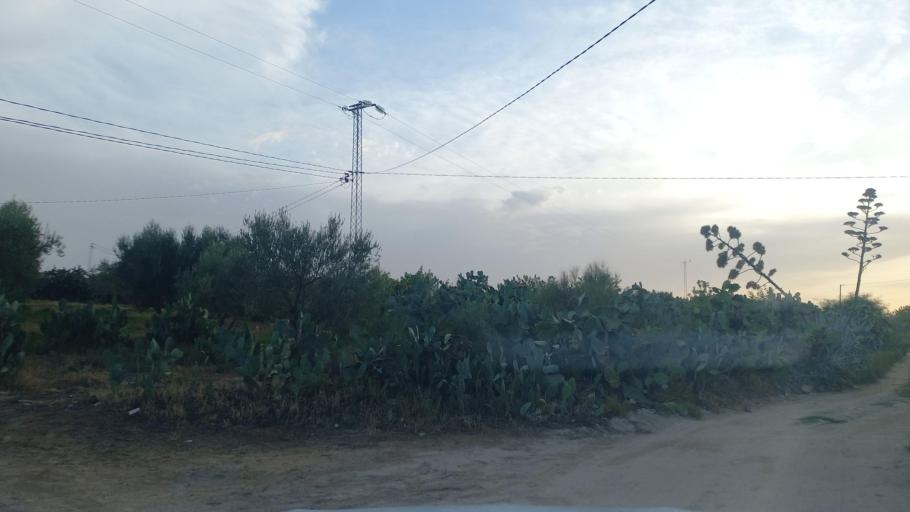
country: TN
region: Al Qasrayn
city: Kasserine
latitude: 35.2161
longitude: 9.0524
